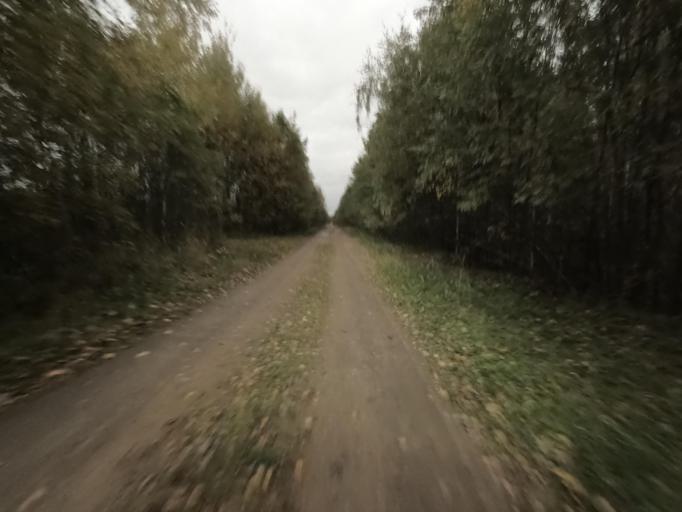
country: RU
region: Leningrad
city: Kirovsk
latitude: 59.8330
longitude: 30.9798
